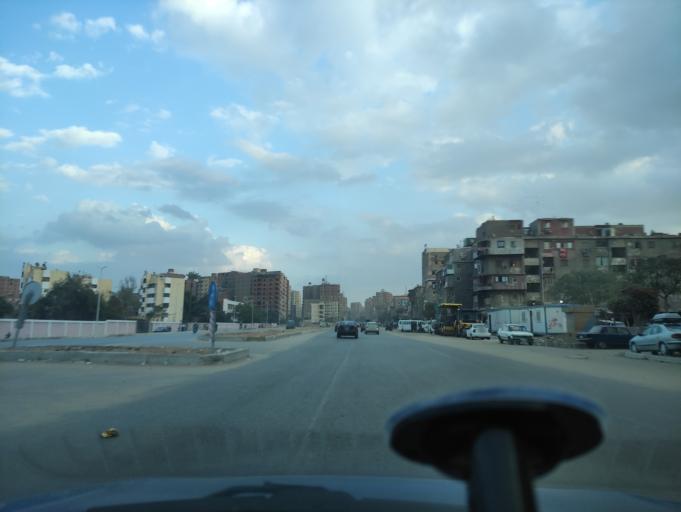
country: EG
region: Muhafazat al Qalyubiyah
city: Al Khankah
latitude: 30.1353
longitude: 31.3538
